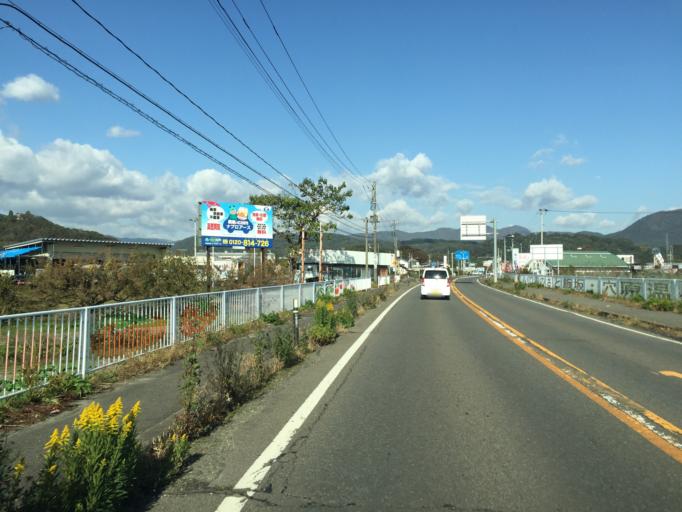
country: JP
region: Fukushima
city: Fukushima-shi
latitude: 37.8161
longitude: 140.4381
